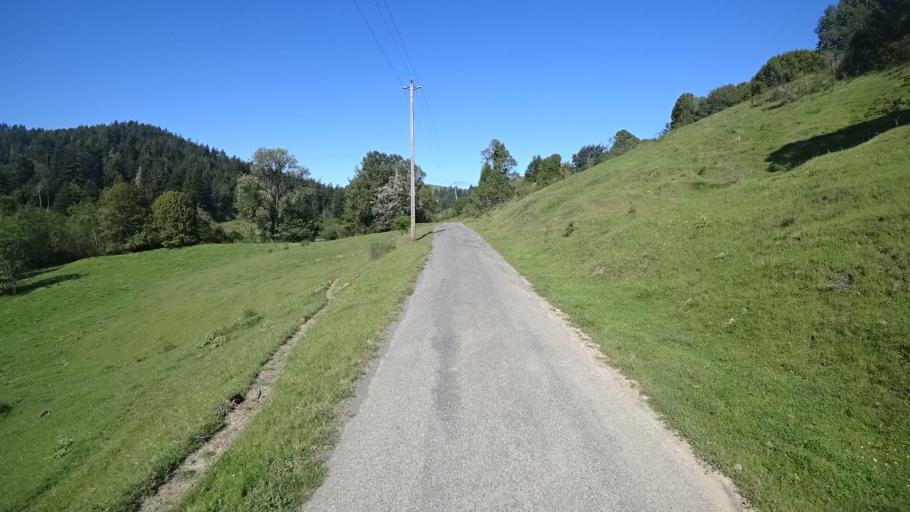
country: US
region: California
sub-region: Humboldt County
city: Fortuna
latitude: 40.5287
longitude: -124.1753
